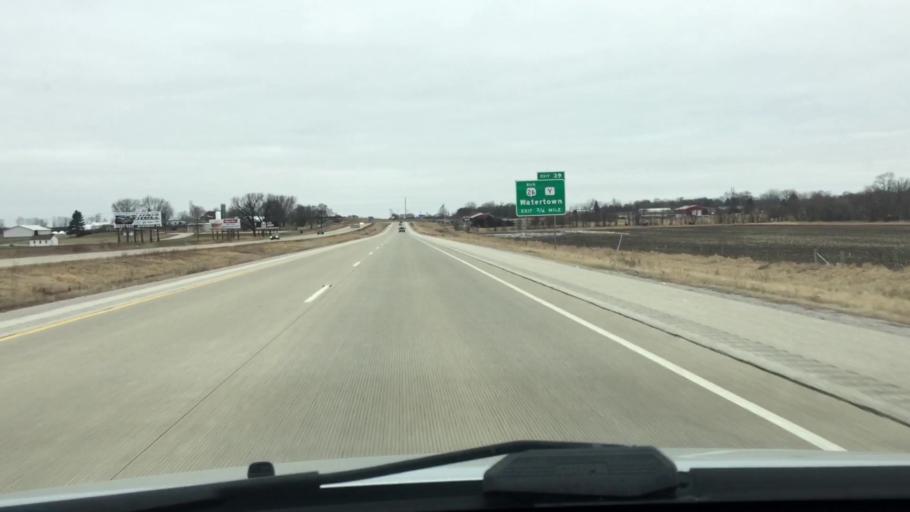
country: US
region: Wisconsin
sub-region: Jefferson County
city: Watertown
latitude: 43.1418
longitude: -88.7349
